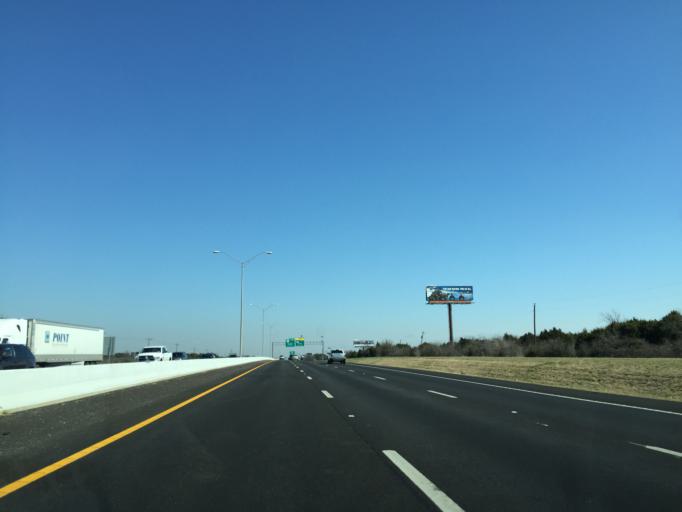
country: US
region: Texas
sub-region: Williamson County
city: Georgetown
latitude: 30.6611
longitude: -97.6723
